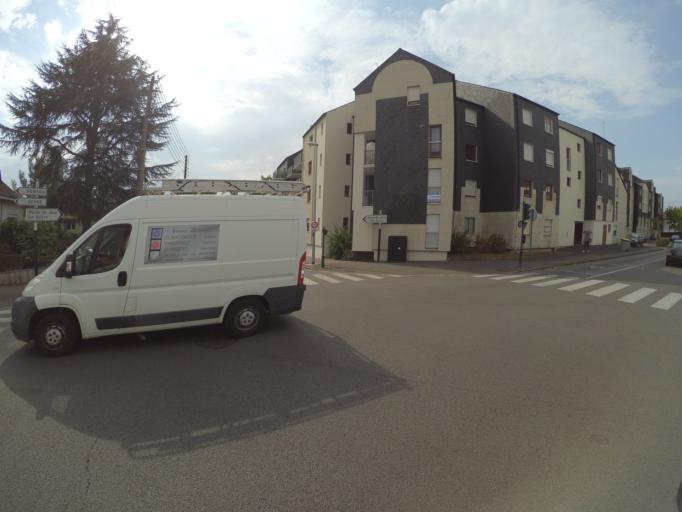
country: FR
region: Pays de la Loire
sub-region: Departement de la Loire-Atlantique
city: Reze
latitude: 47.1882
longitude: -1.5306
